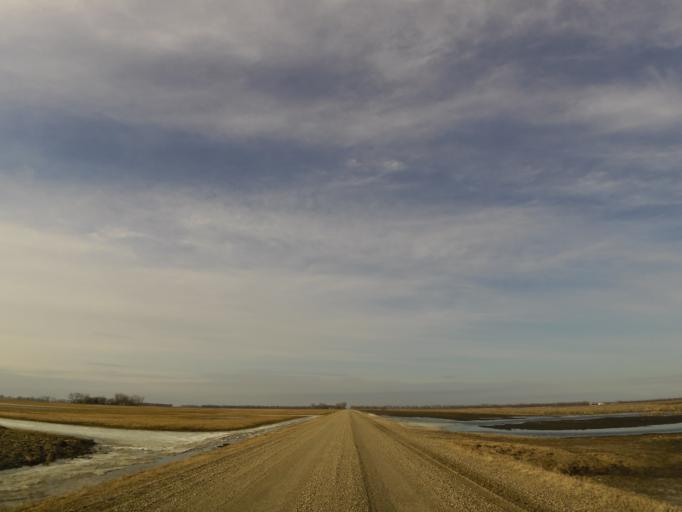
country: US
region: North Dakota
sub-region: Walsh County
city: Grafton
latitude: 48.4190
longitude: -97.2121
